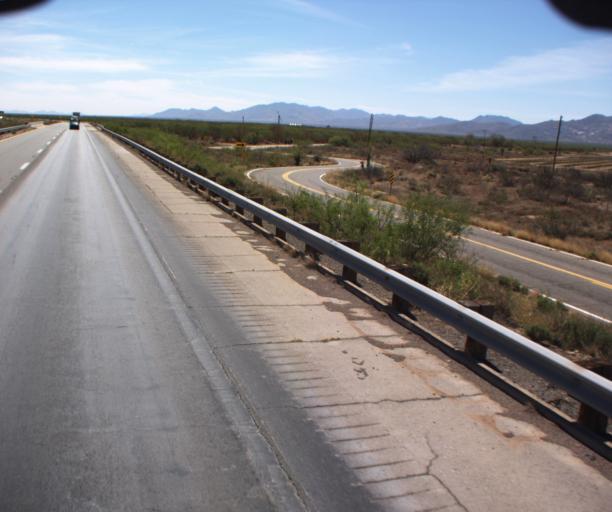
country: US
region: Arizona
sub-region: Cochise County
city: Willcox
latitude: 32.3227
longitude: -109.5026
